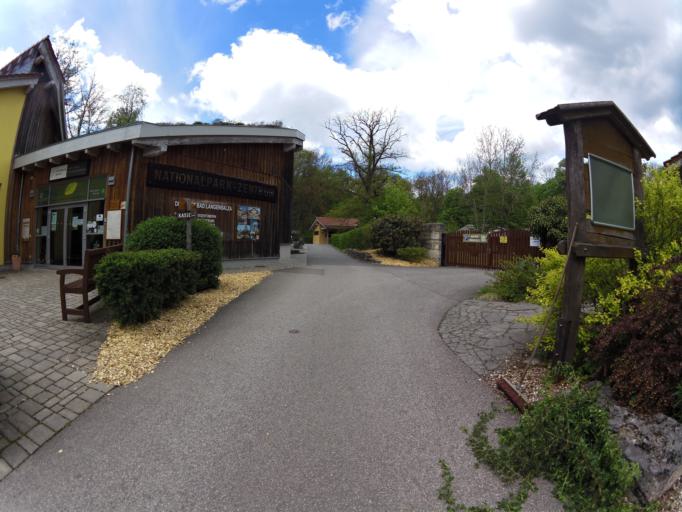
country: DE
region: Thuringia
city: Weberstedt
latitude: 51.0822
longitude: 10.5145
